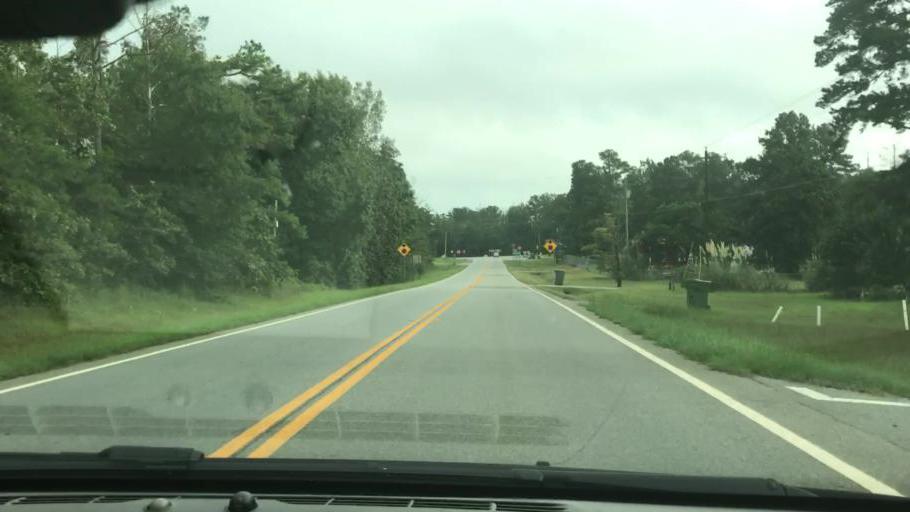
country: US
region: Georgia
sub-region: Quitman County
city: Georgetown
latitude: 31.8579
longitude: -85.0695
